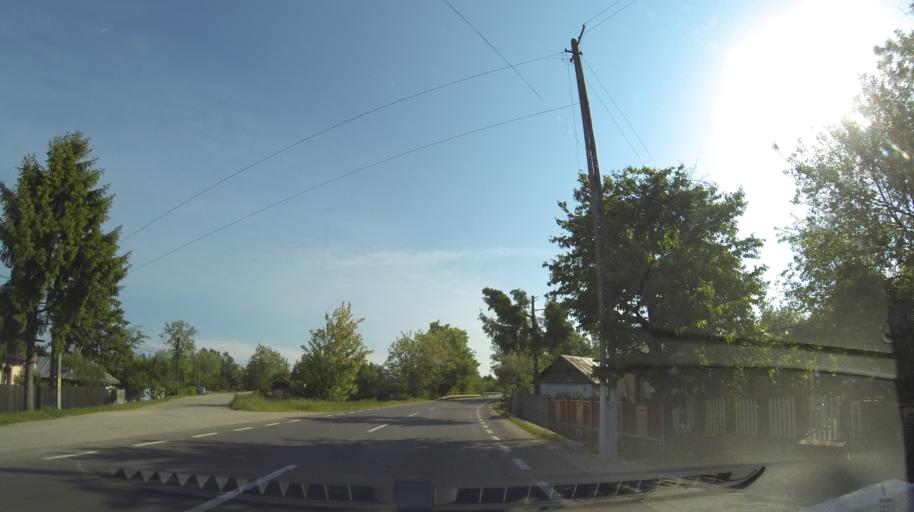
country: RO
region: Arges
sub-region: Comuna Lunca Corbului
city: Lunca Corbului
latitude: 44.6796
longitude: 24.7542
